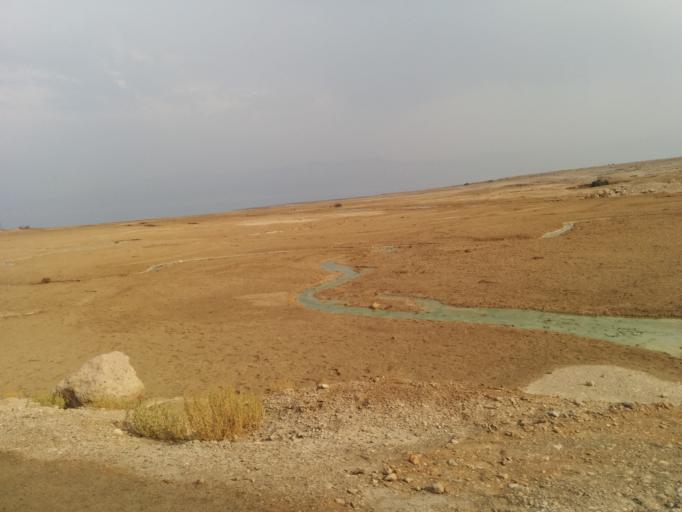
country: PS
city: `Arab ar Rashaydah
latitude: 31.4189
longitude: 35.3804
